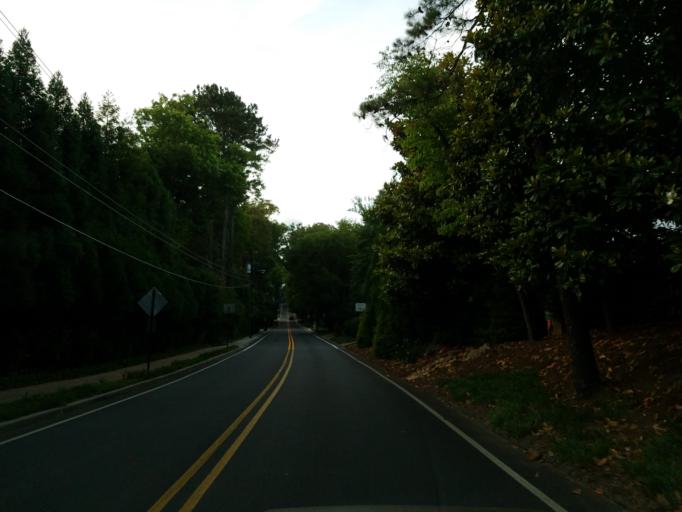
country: US
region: Georgia
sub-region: Fulton County
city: Sandy Springs
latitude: 33.8778
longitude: -84.3973
